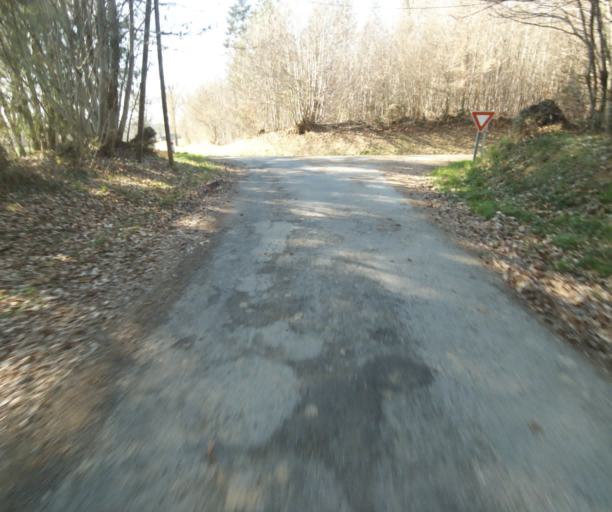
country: FR
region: Limousin
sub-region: Departement de la Correze
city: Seilhac
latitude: 45.3897
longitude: 1.7286
